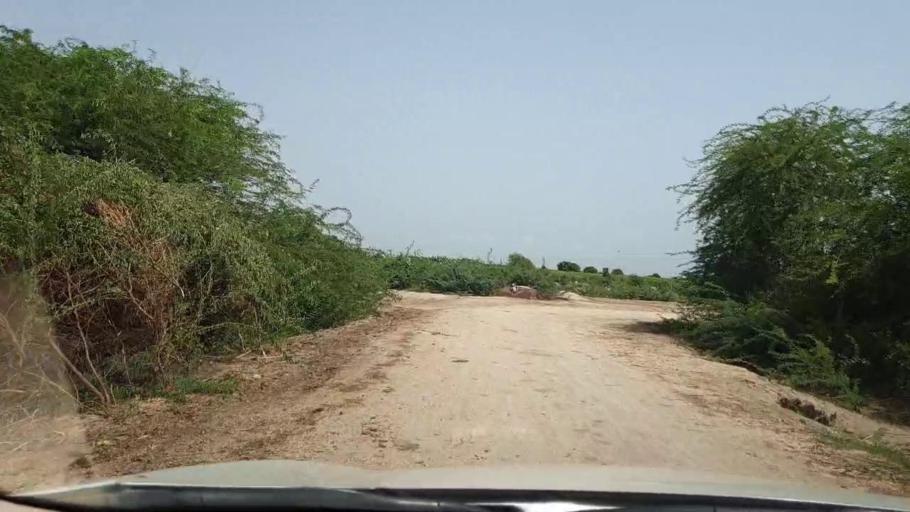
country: PK
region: Sindh
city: Tando Ghulam Ali
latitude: 25.2298
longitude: 68.9164
